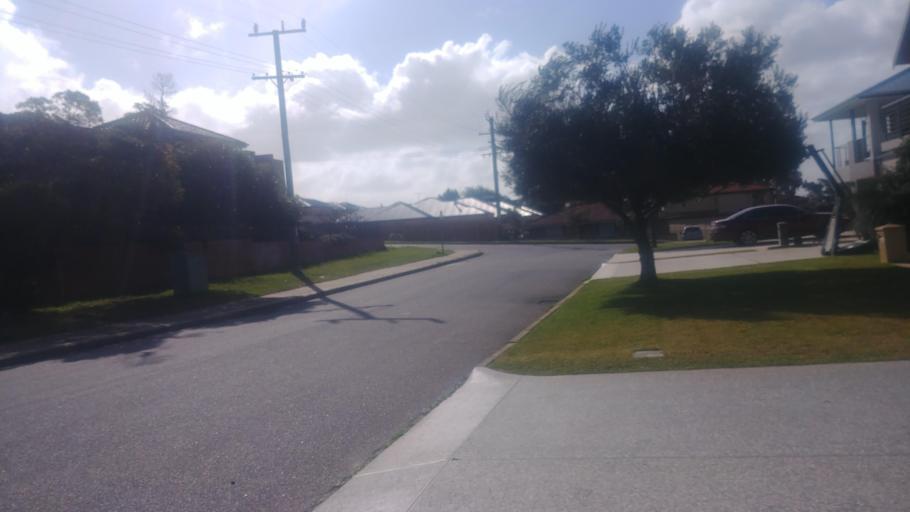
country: AU
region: Western Australia
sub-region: Fremantle
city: South Fremantle
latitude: -32.0681
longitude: 115.7627
